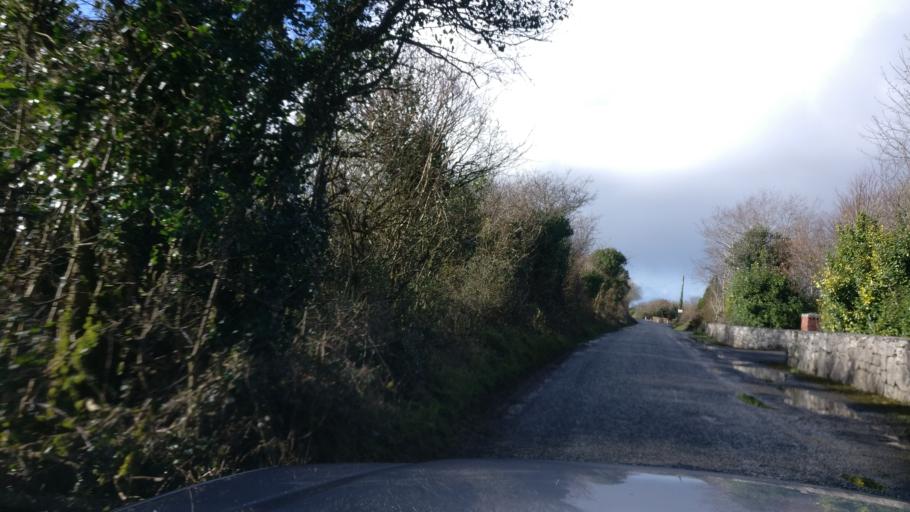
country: IE
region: Connaught
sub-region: County Galway
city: Athenry
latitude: 53.2385
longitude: -8.8030
